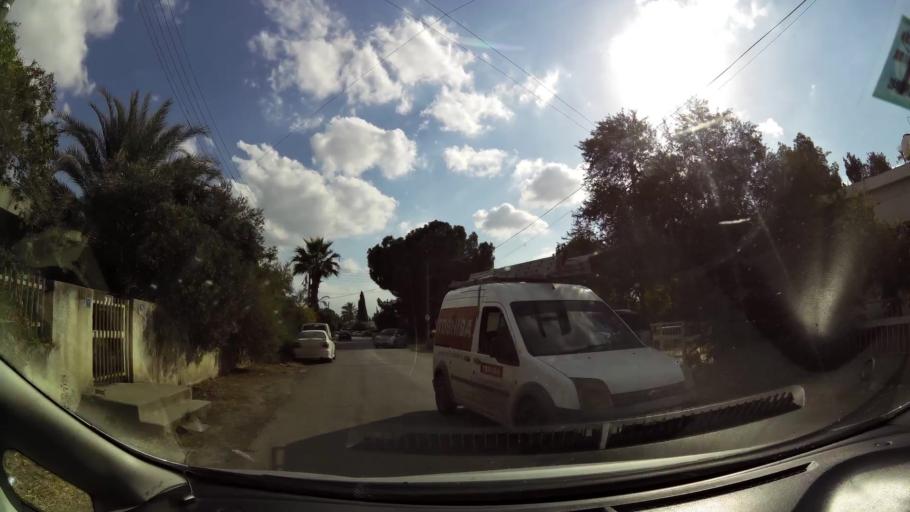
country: CY
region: Lefkosia
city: Nicosia
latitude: 35.1966
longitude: 33.3563
